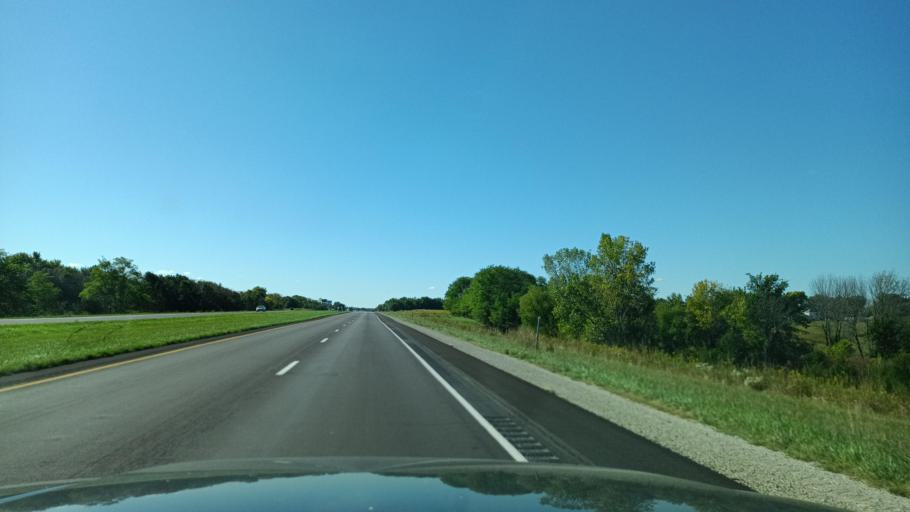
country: US
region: Illinois
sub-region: Hancock County
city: Nauvoo
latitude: 40.4837
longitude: -91.4444
